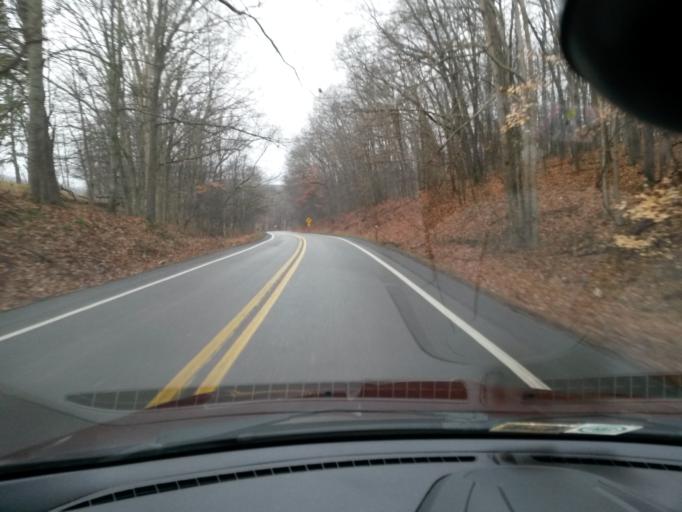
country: US
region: West Virginia
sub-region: Greenbrier County
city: Lewisburg
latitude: 37.8697
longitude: -80.5467
